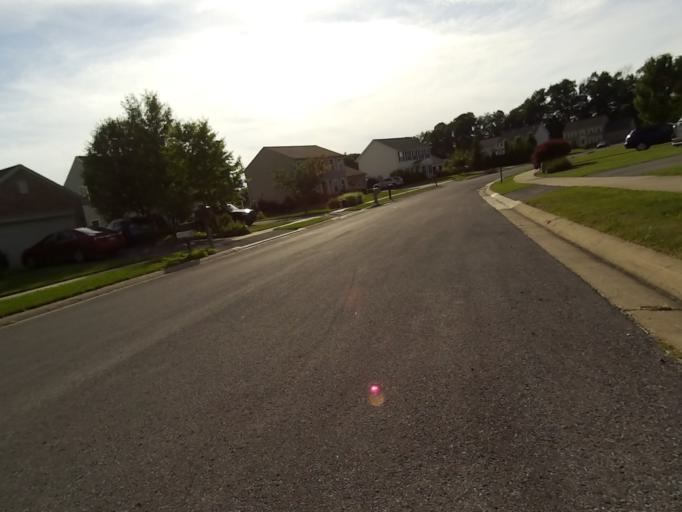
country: US
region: Pennsylvania
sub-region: Centre County
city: Park Forest Village
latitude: 40.8100
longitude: -77.9474
